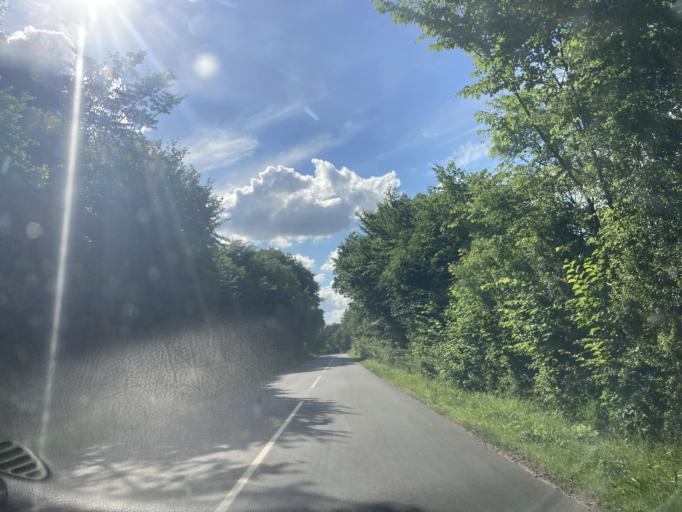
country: DK
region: South Denmark
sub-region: Kolding Kommune
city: Kolding
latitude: 55.4843
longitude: 9.4050
